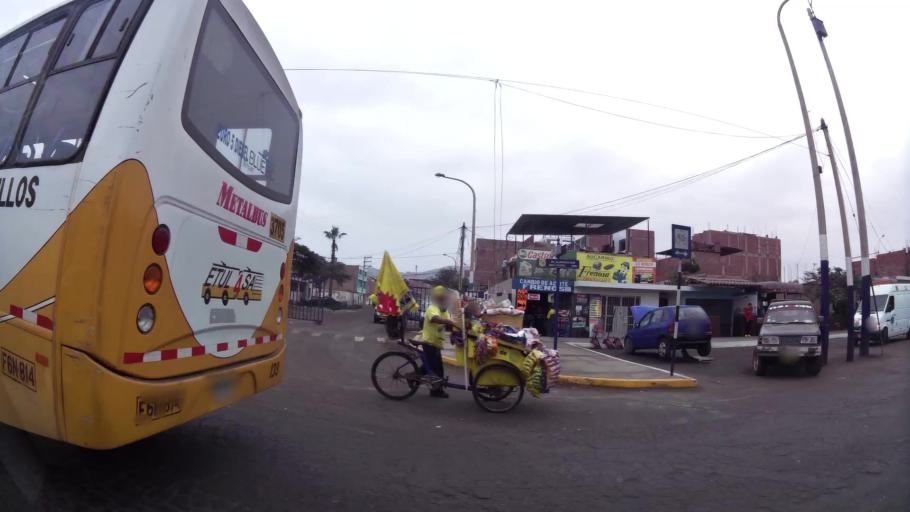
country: PE
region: Lima
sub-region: Lima
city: Surco
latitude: -12.2030
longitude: -77.0161
